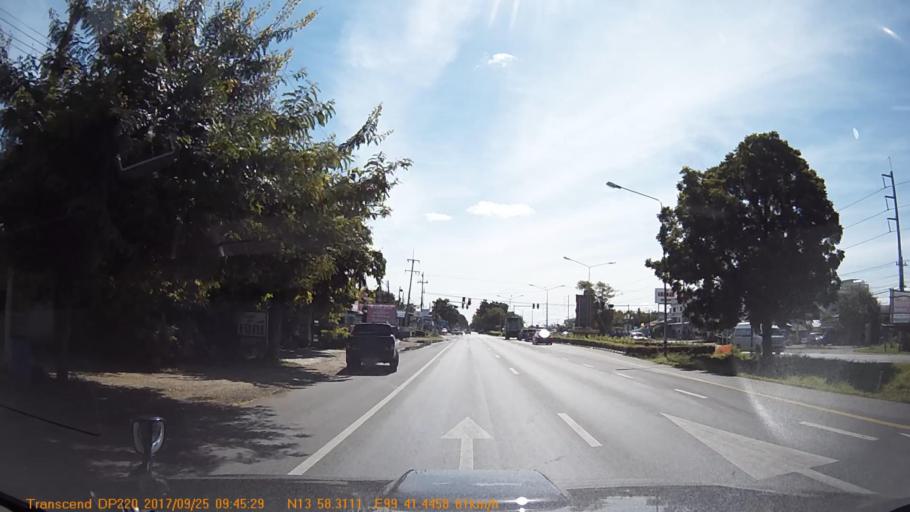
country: TH
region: Kanchanaburi
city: Tha Muang
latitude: 13.9718
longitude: 99.6909
